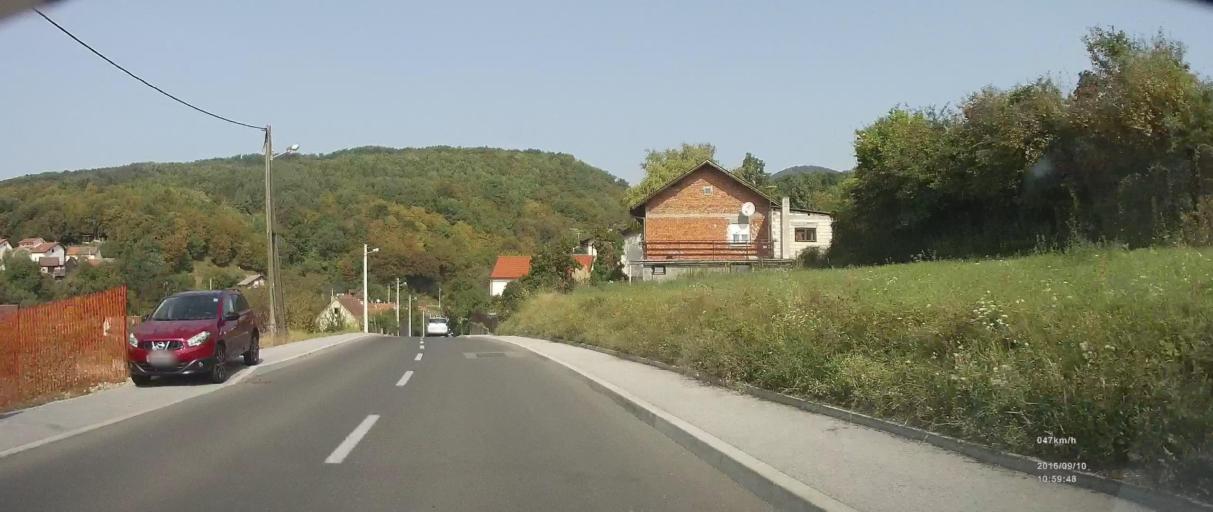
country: HR
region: Grad Zagreb
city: Zagreb
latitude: 45.8512
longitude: 15.9370
